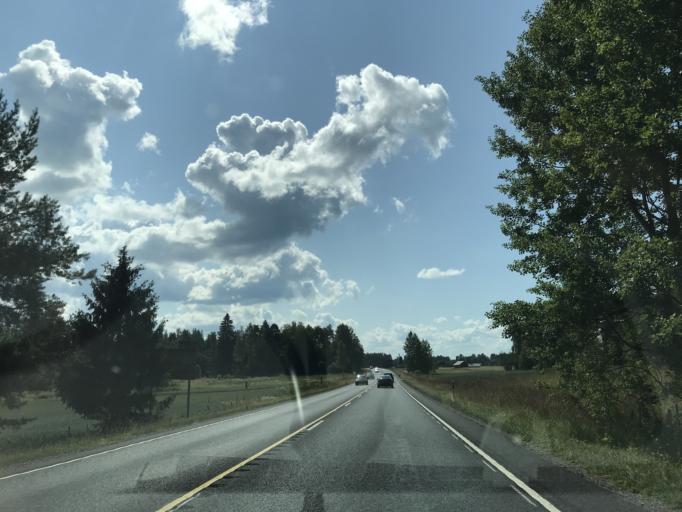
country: FI
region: Paijanne Tavastia
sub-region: Lahti
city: Lahti
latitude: 61.1046
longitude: 25.6417
